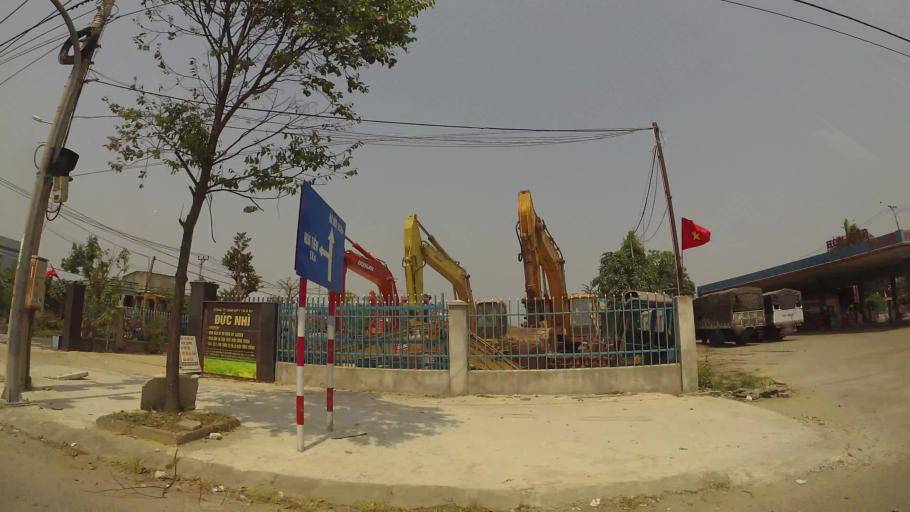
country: VN
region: Da Nang
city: Cam Le
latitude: 15.9931
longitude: 108.1937
